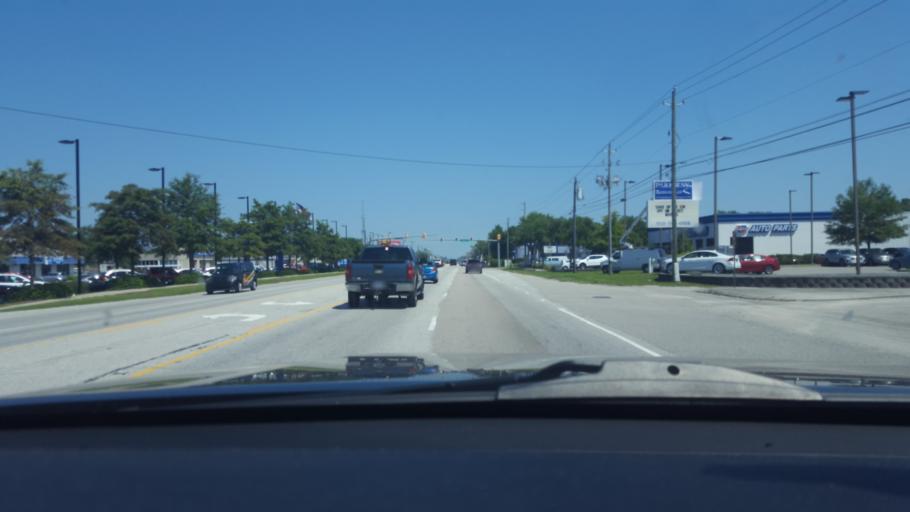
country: US
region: North Carolina
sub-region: New Hanover County
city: Kings Grant
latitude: 34.2500
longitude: -77.8583
